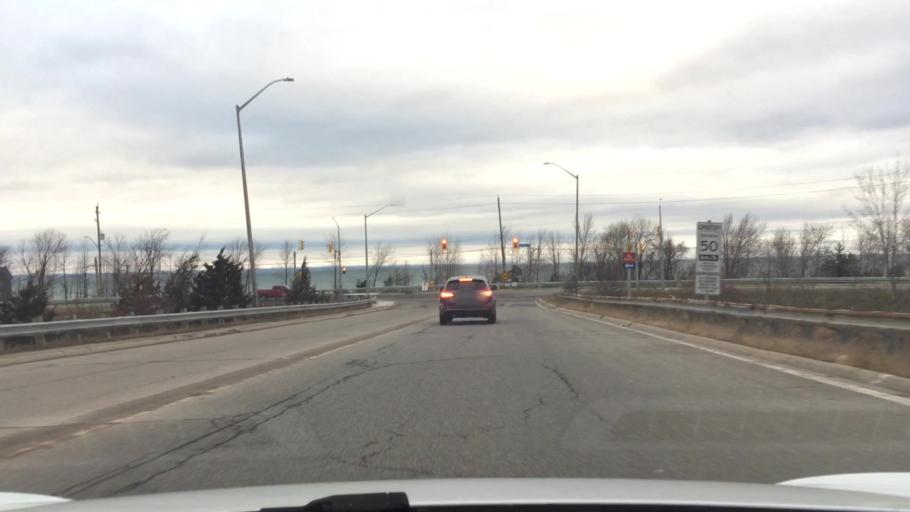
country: CA
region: Ontario
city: Oakville
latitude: 43.2090
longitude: -79.5955
